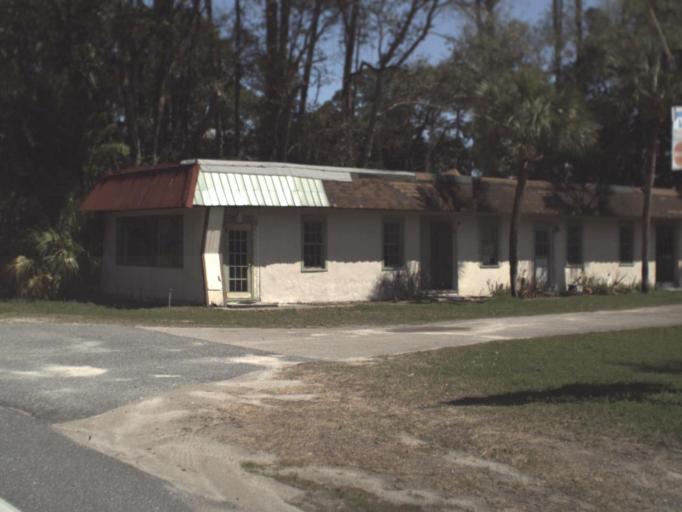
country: US
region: Florida
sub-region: Wakulla County
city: Crawfordville
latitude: 30.0366
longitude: -84.3884
